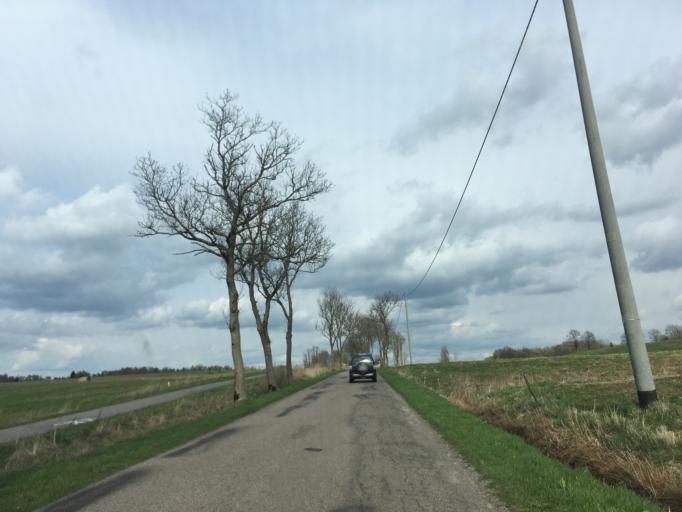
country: PL
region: Podlasie
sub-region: Powiat suwalski
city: Filipow
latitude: 54.3592
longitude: 22.7823
